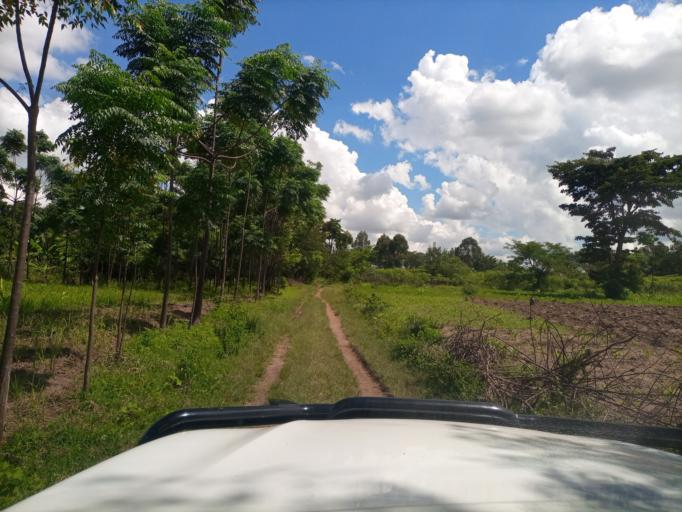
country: UG
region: Eastern Region
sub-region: Tororo District
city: Tororo
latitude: 0.7219
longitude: 34.0222
